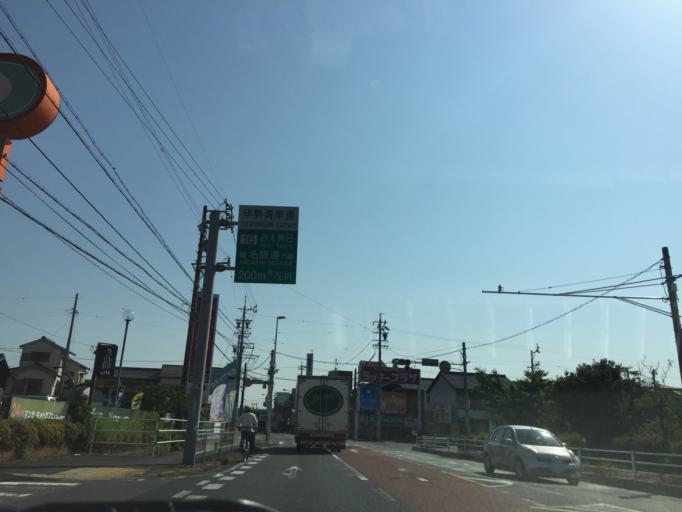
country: JP
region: Mie
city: Yokkaichi
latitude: 35.0096
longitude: 136.6564
